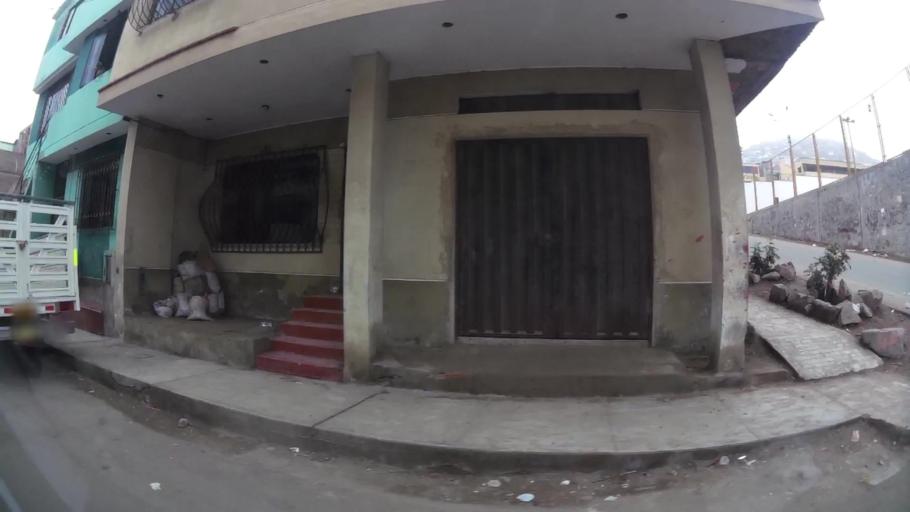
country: PE
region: Lima
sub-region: Lima
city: Surco
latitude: -12.1519
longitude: -76.9638
